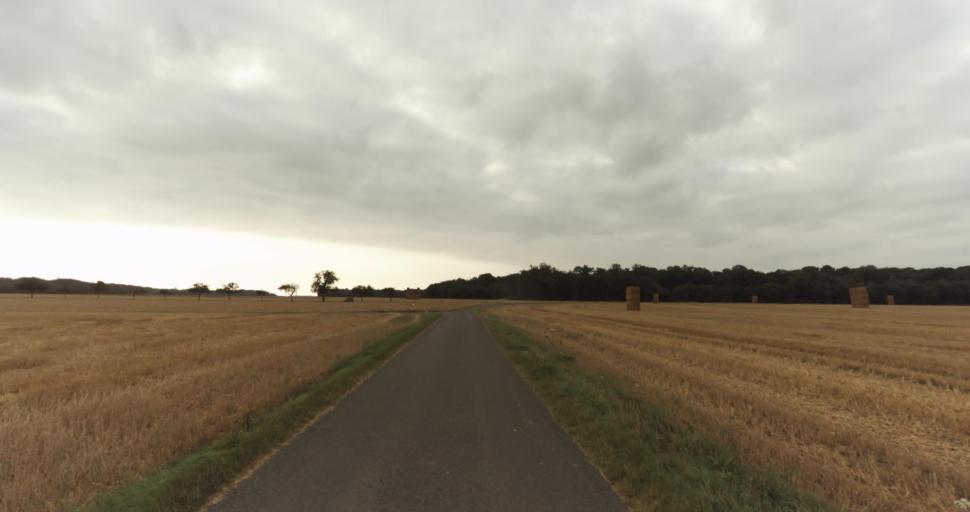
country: FR
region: Haute-Normandie
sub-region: Departement de l'Eure
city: Saint-Germain-sur-Avre
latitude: 48.8033
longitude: 1.2863
